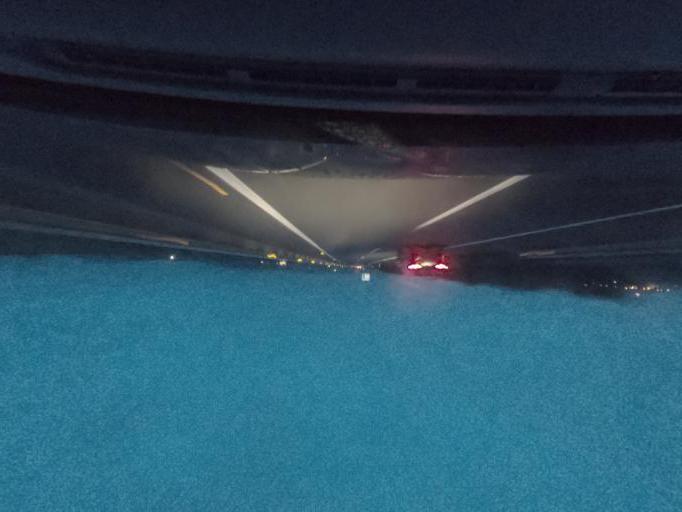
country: ES
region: Extremadura
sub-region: Provincia de Caceres
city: Torreorgaz
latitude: 39.3786
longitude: -6.3422
